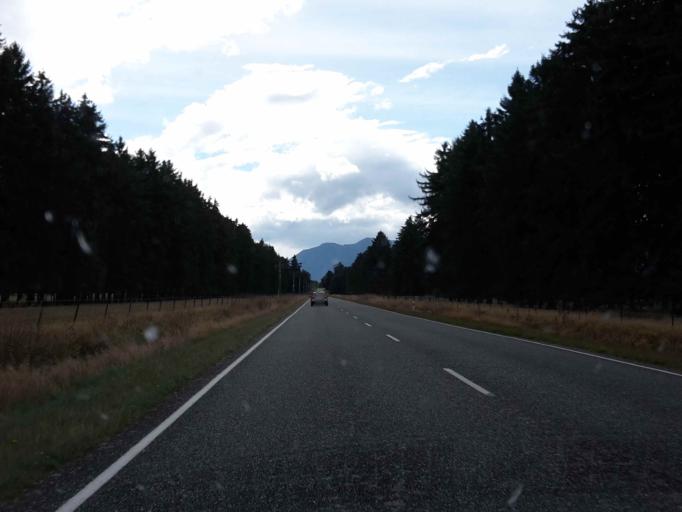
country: NZ
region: Otago
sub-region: Queenstown-Lakes District
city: Wanaka
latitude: -44.7285
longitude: 169.1369
